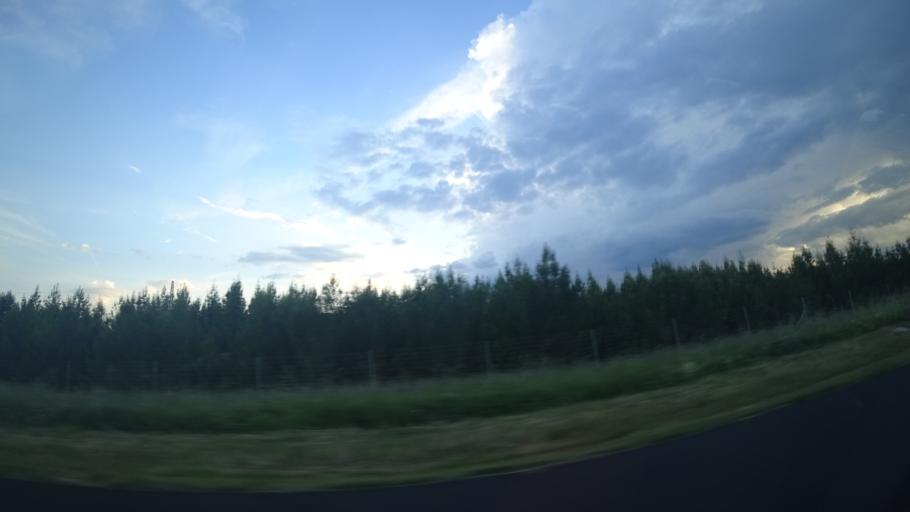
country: FR
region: Languedoc-Roussillon
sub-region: Departement de l'Herault
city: Aspiran
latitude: 43.5835
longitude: 3.4655
